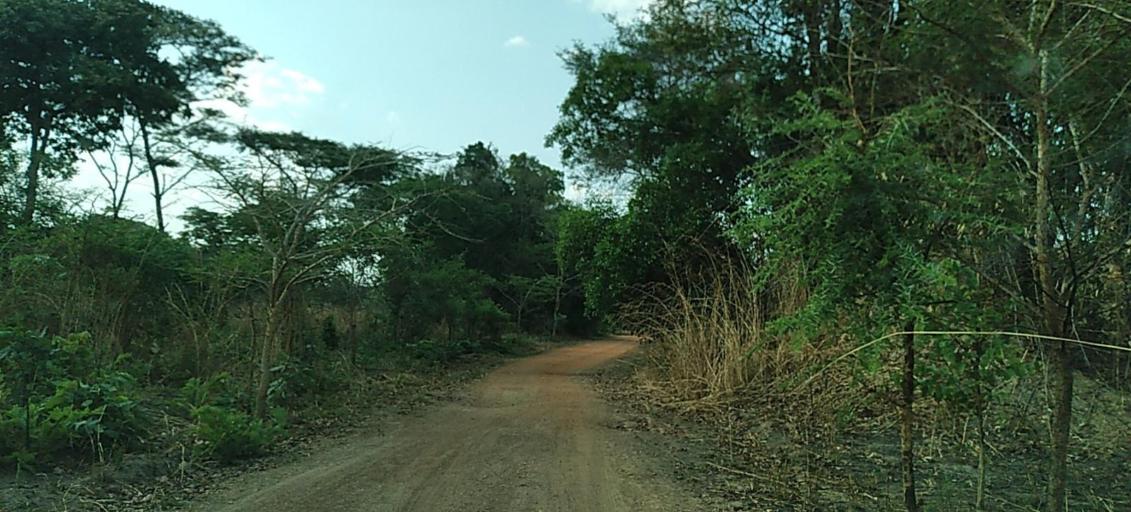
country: ZM
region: Copperbelt
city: Mpongwe
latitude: -13.4684
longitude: 28.0695
